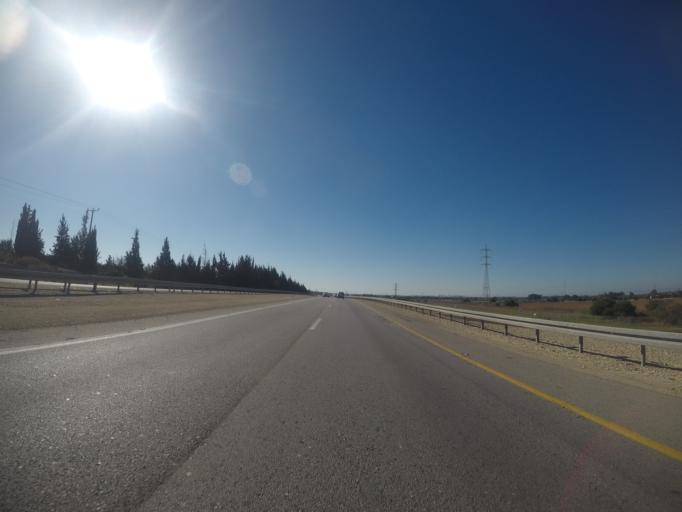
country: IL
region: Southern District
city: Ashdod
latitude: 31.7336
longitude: 34.6409
